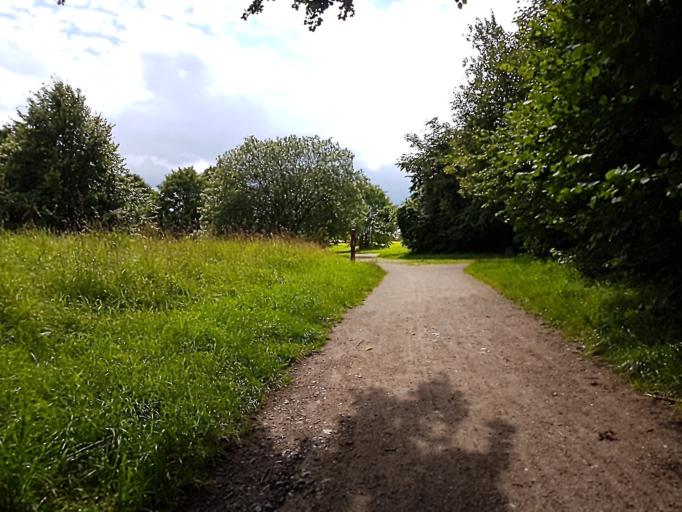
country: DK
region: Capital Region
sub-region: Fureso Kommune
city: Vaerlose
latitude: 55.7910
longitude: 12.3585
